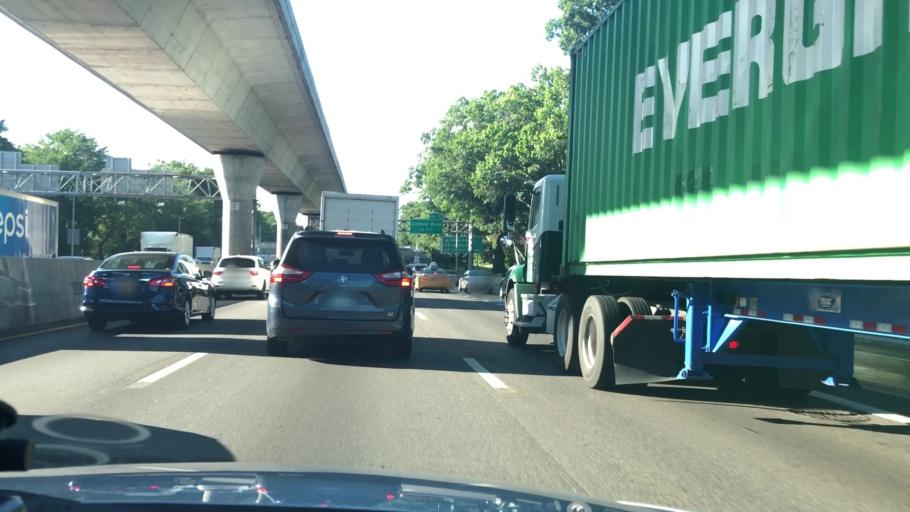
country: US
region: New York
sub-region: Queens County
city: Jamaica
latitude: 40.6890
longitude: -73.8091
